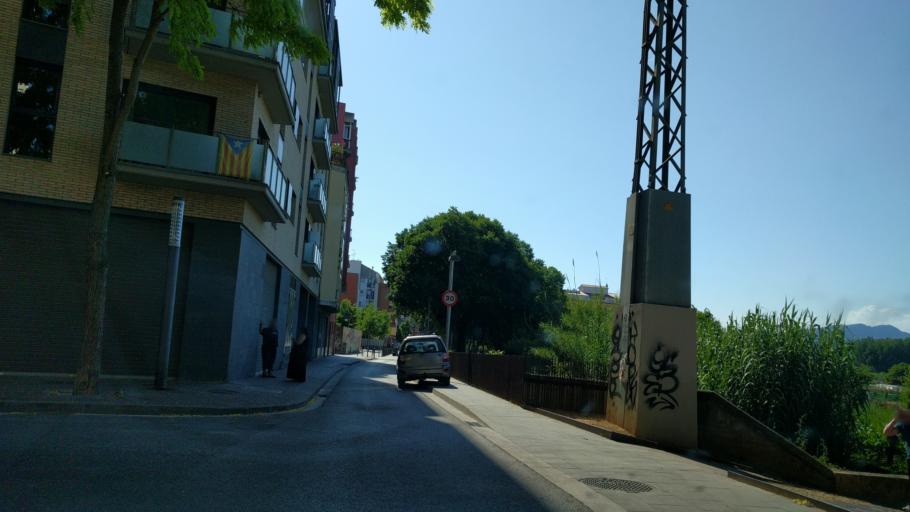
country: ES
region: Catalonia
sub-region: Provincia de Girona
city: Salt
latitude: 41.9774
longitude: 2.8025
